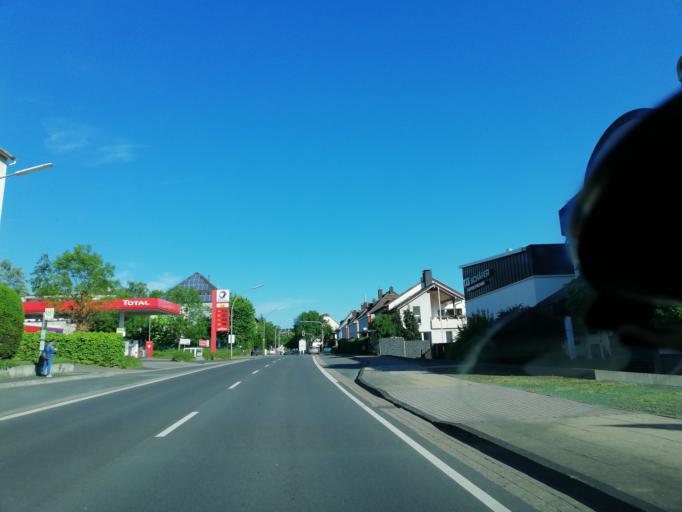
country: DE
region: North Rhine-Westphalia
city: Wetter (Ruhr)
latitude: 51.3965
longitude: 7.3526
